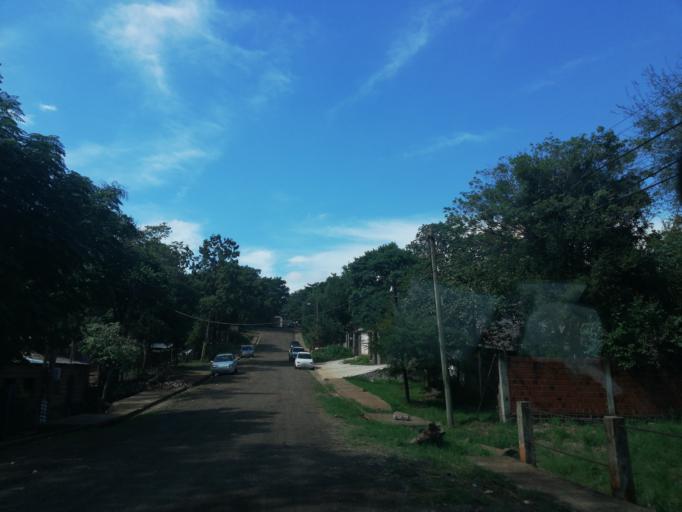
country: AR
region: Misiones
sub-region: Departamento de Capital
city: Posadas
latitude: -27.3645
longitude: -55.9104
